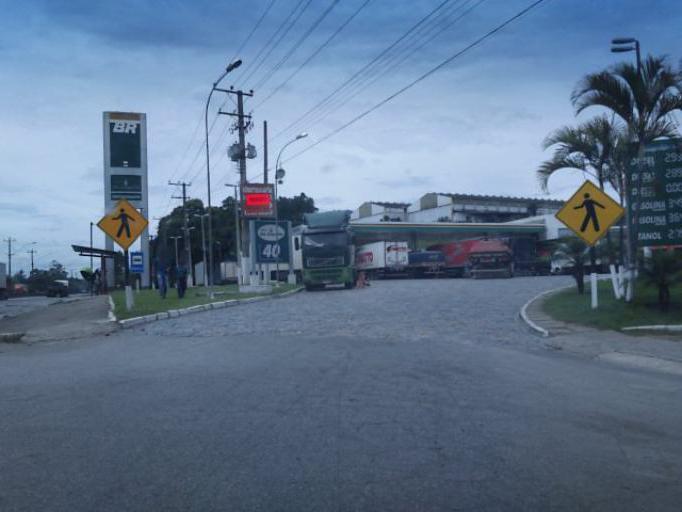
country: BR
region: Sao Paulo
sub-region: Itapecerica Da Serra
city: Itapecerica da Serra
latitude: -23.7485
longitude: -46.9009
